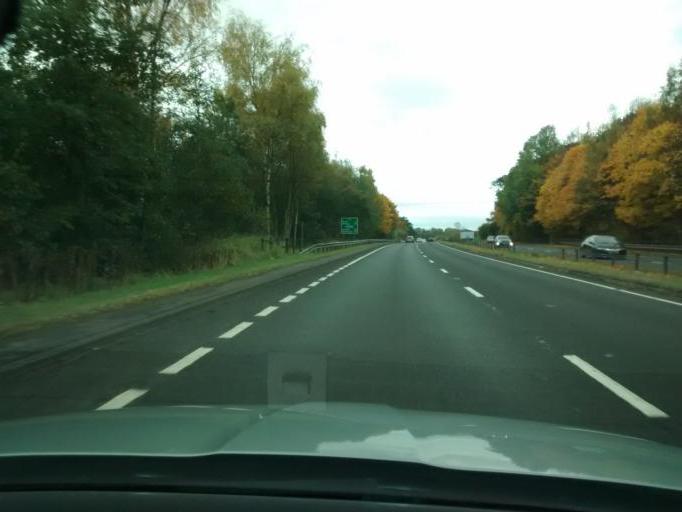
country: GB
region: Scotland
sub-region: Perth and Kinross
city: Luncarty
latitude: 56.4427
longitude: -3.4718
